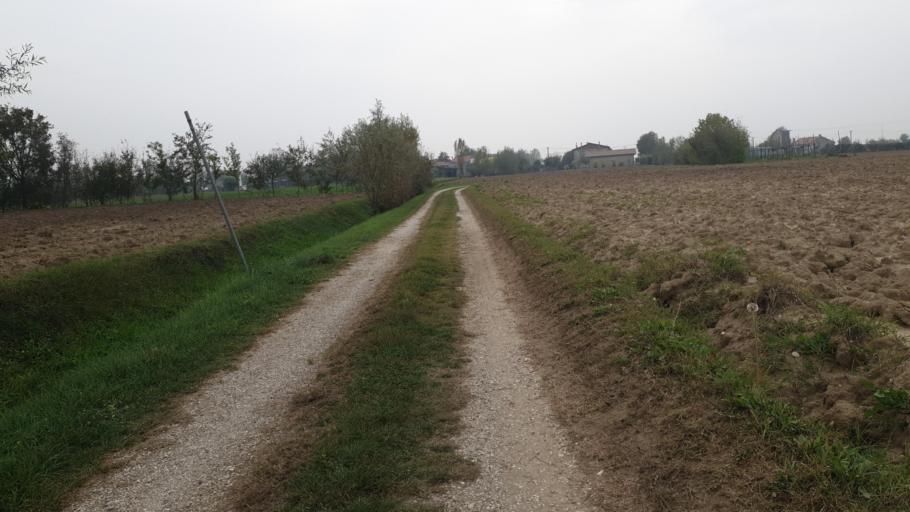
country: IT
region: Veneto
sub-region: Provincia di Padova
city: Bovolenta
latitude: 45.2899
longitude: 11.9215
